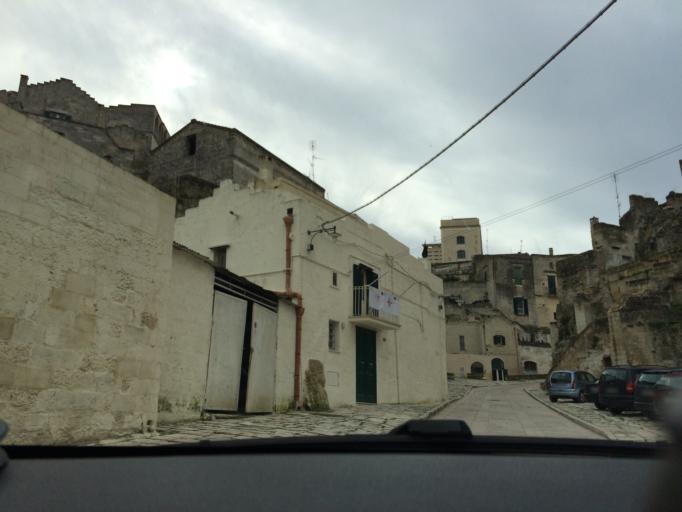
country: IT
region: Basilicate
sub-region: Provincia di Matera
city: Matera
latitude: 40.6627
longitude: 16.6115
